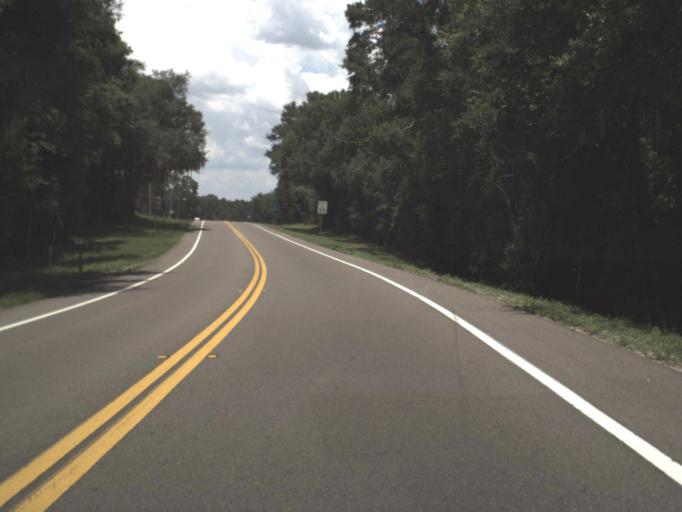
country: US
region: Florida
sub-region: Alachua County
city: Gainesville
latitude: 29.6540
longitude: -82.2586
